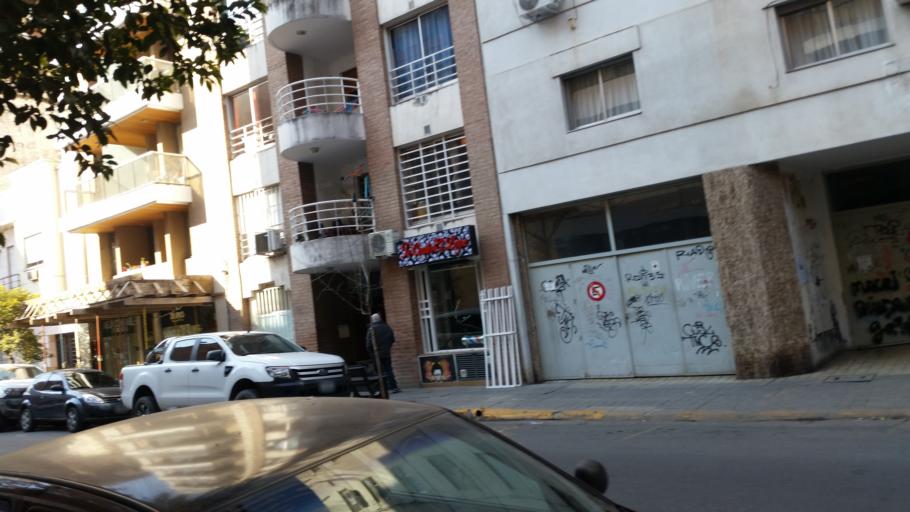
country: AR
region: Cordoba
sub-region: Departamento de Capital
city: Cordoba
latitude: -31.4294
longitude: -64.1895
